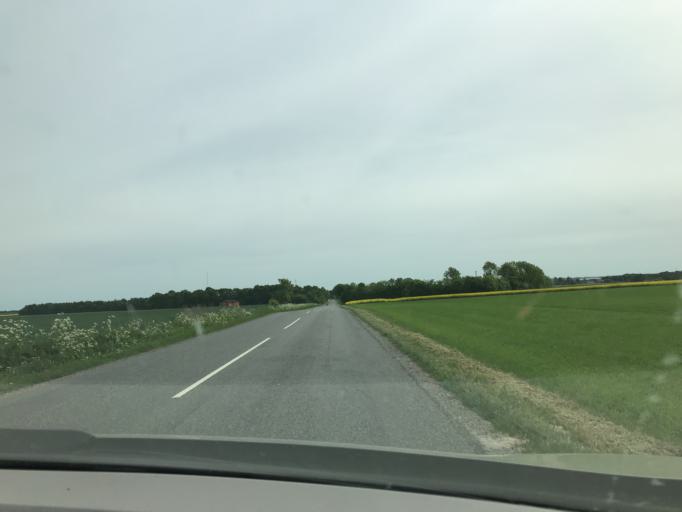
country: DK
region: Central Jutland
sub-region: Norddjurs Kommune
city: Allingabro
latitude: 56.5144
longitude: 10.3306
